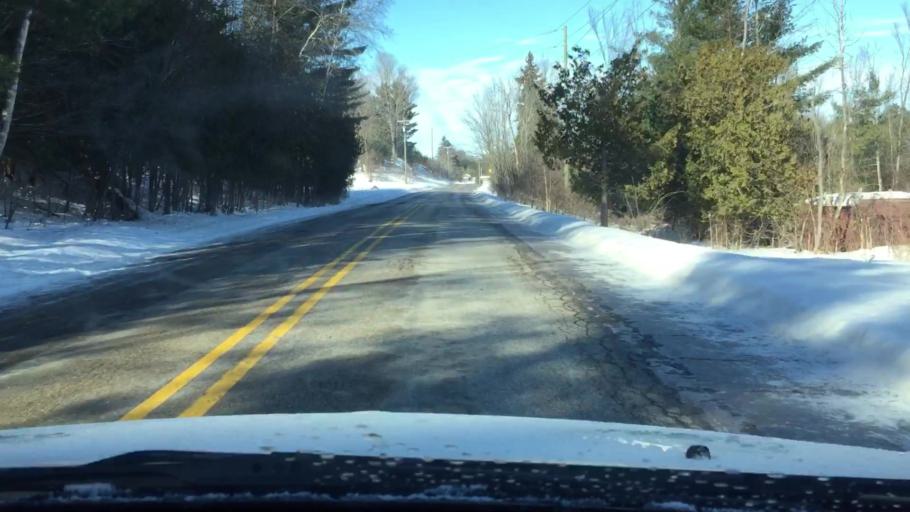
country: US
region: Michigan
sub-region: Charlevoix County
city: East Jordan
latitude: 45.1089
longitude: -85.1290
